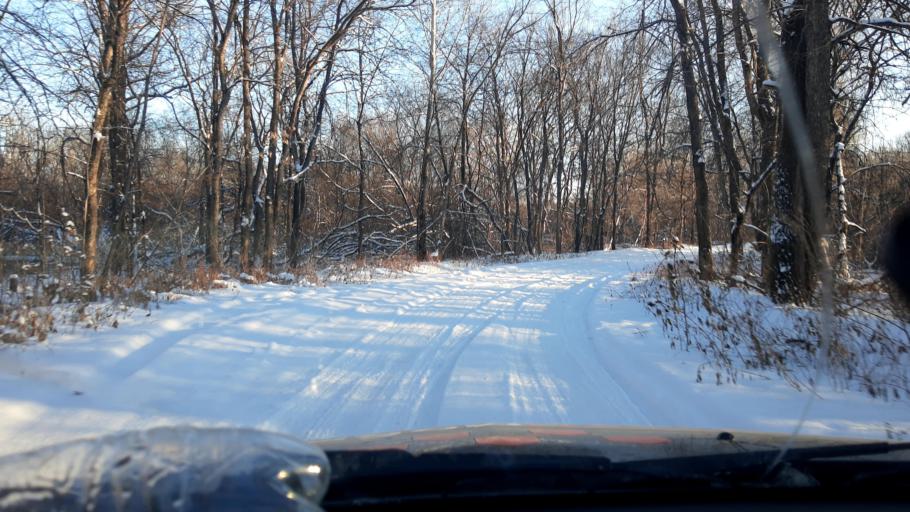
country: RU
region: Bashkortostan
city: Ufa
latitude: 54.6616
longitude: 55.9629
